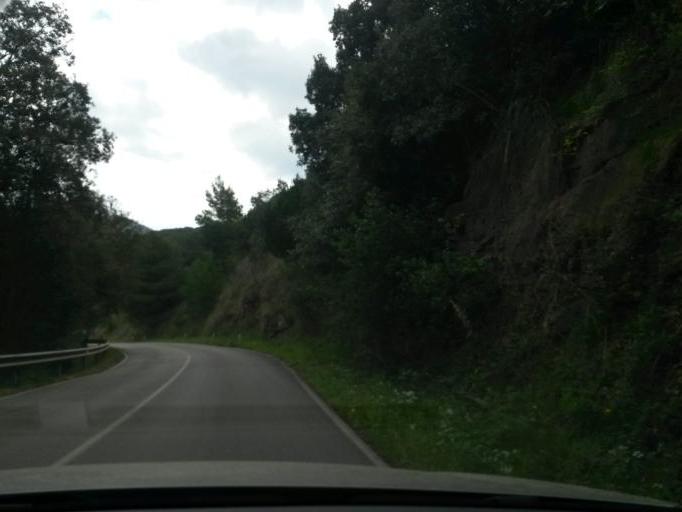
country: IT
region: Tuscany
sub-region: Provincia di Livorno
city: Rio nell'Elba
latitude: 42.8092
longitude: 10.3609
